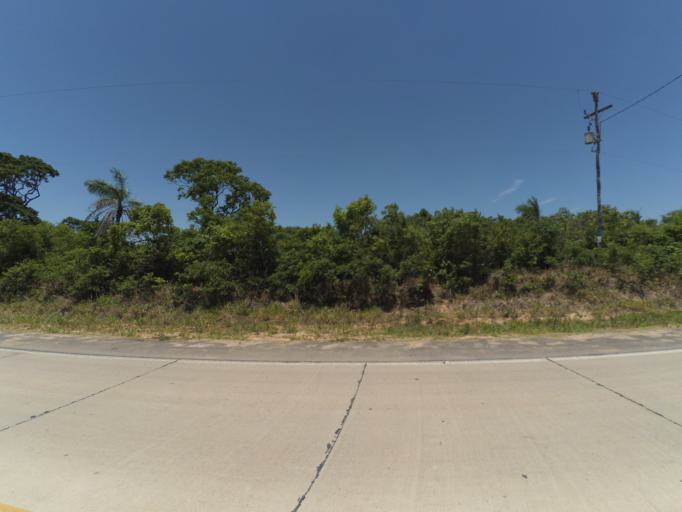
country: BO
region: Santa Cruz
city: Santa Cruz de la Sierra
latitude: -17.7824
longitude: -63.2590
